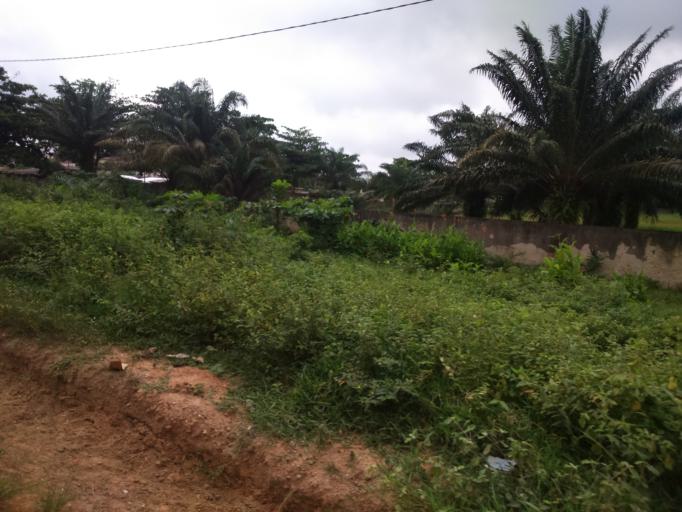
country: CI
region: Agneby
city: Agboville
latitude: 6.0123
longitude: -4.1461
